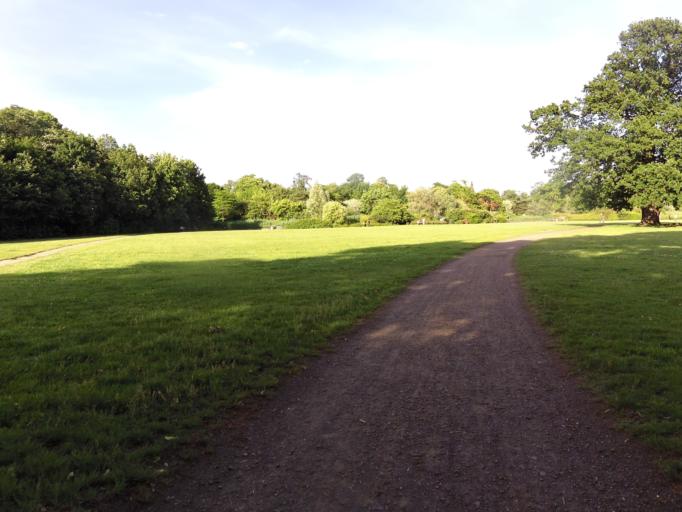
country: DE
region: Saxony
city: Leipzig
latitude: 51.3513
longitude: 12.3620
